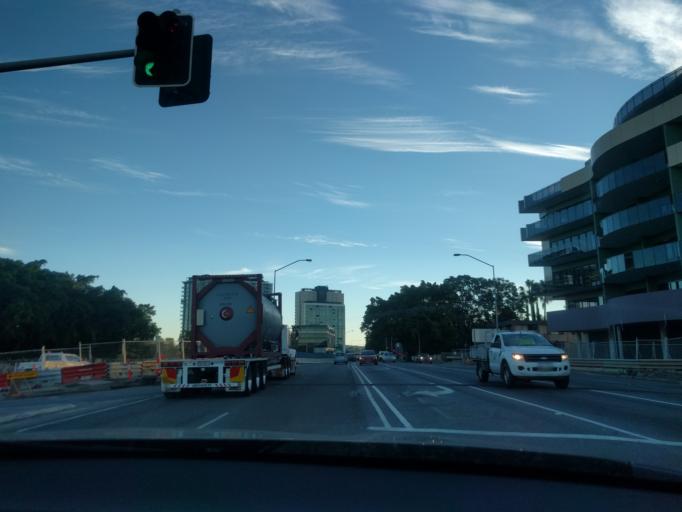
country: AU
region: Queensland
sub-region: Brisbane
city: Ascot
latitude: -27.4375
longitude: 153.0708
